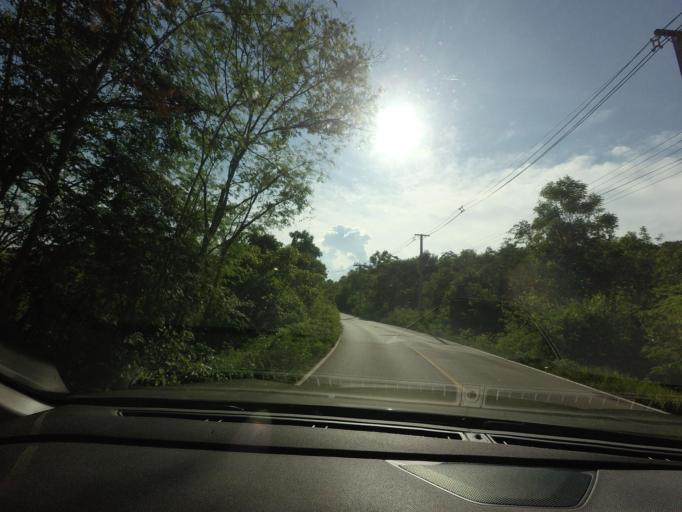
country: TH
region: Prachuap Khiri Khan
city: Pran Buri
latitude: 12.4118
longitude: 99.9735
